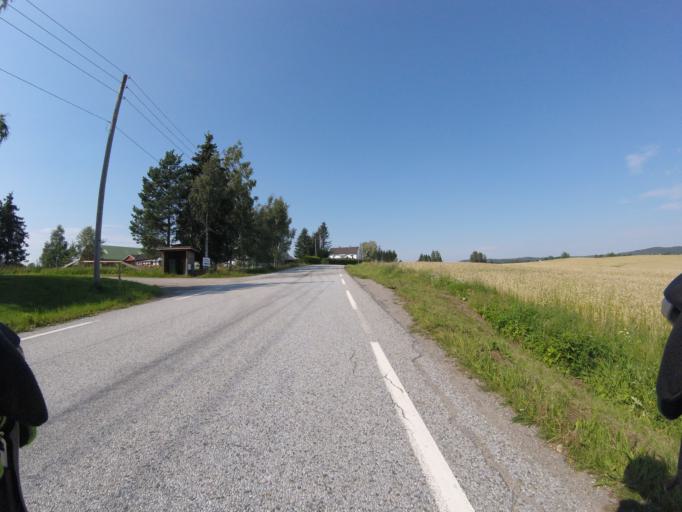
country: NO
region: Akershus
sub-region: Ullensaker
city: Klofta
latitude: 60.0861
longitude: 11.1626
